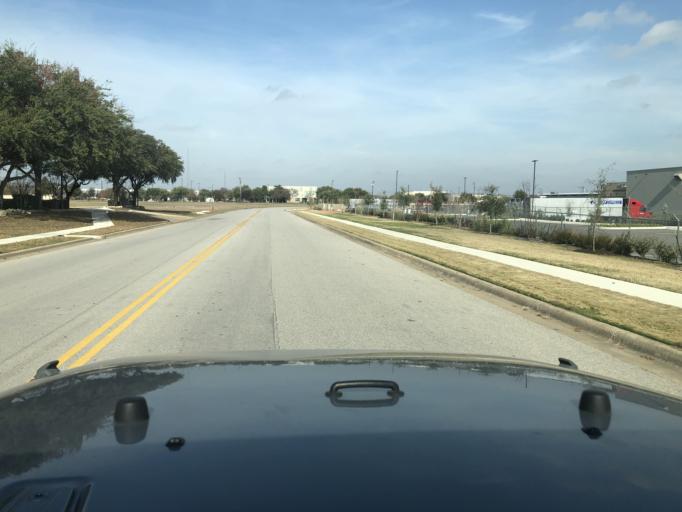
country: US
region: Texas
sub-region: Williamson County
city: Round Rock
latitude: 30.5320
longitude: -97.6808
